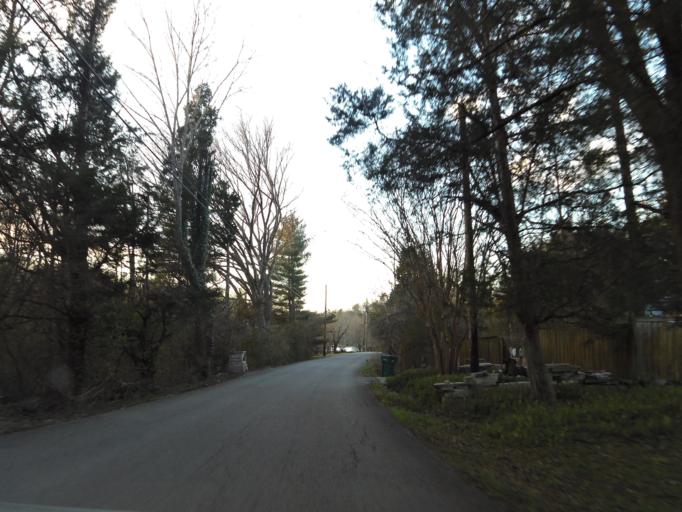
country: US
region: Tennessee
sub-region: Knox County
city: Knoxville
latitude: 35.9180
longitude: -83.9447
